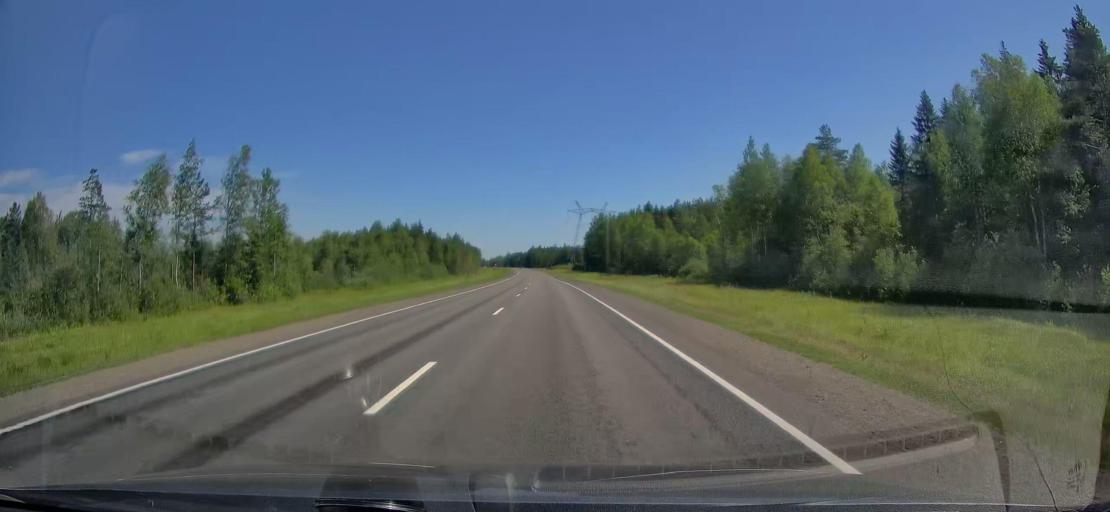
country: RU
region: Tverskaya
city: Ves'yegonsk
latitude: 58.9221
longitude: 37.2221
